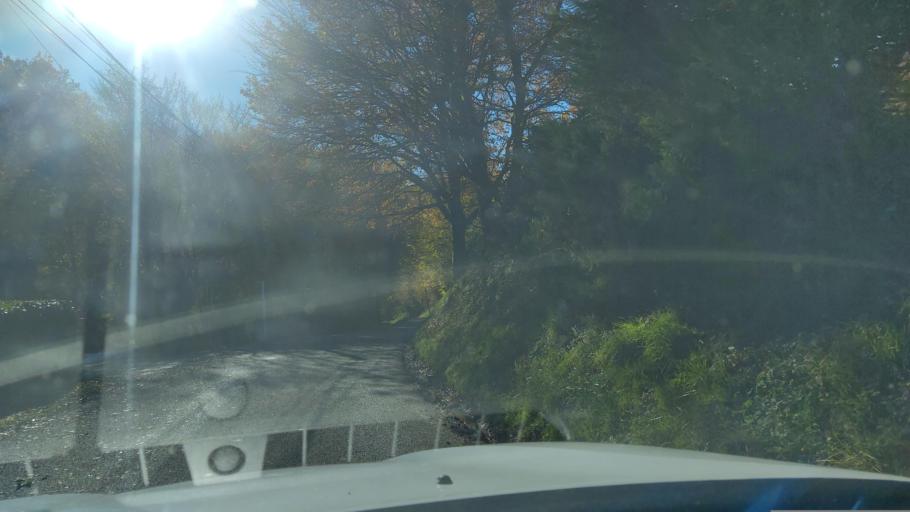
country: FR
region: Rhone-Alpes
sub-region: Departement de la Savoie
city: Vimines
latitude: 45.5093
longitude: 5.8424
